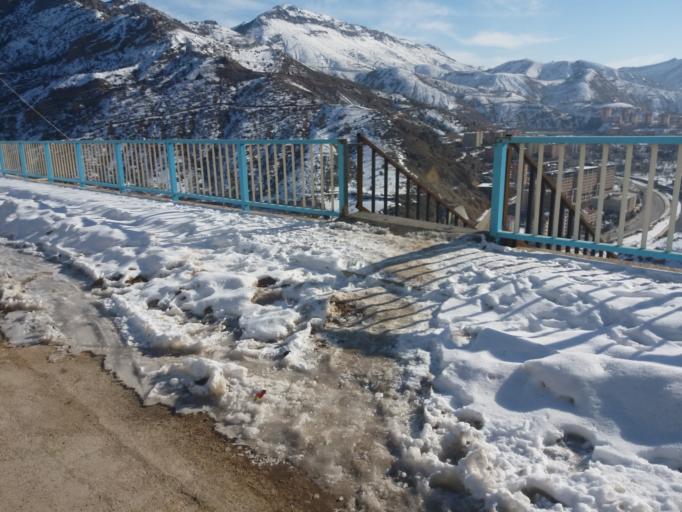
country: TR
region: Gumushane
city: Gumushkhane
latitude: 40.4404
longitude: 39.4993
